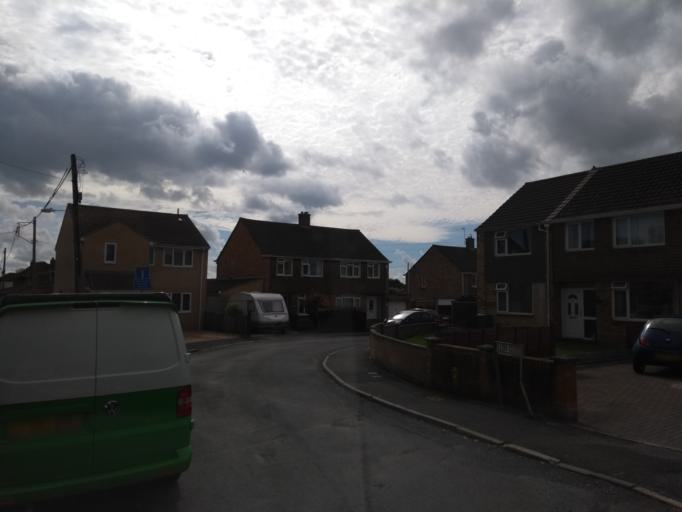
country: GB
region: England
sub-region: Somerset
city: North Petherton
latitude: 51.0927
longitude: -3.0125
